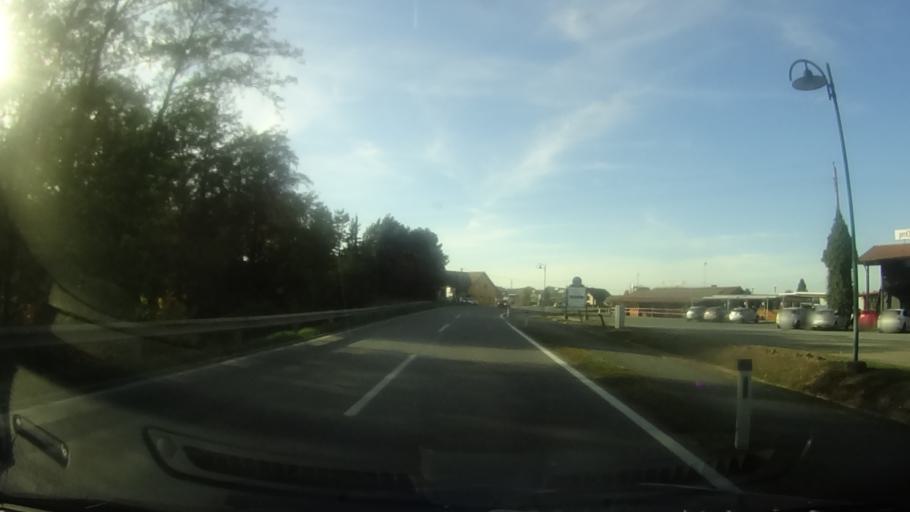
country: AT
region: Styria
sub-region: Politischer Bezirk Leibnitz
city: Kaindorf an der Sulm
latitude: 46.8059
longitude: 15.5321
